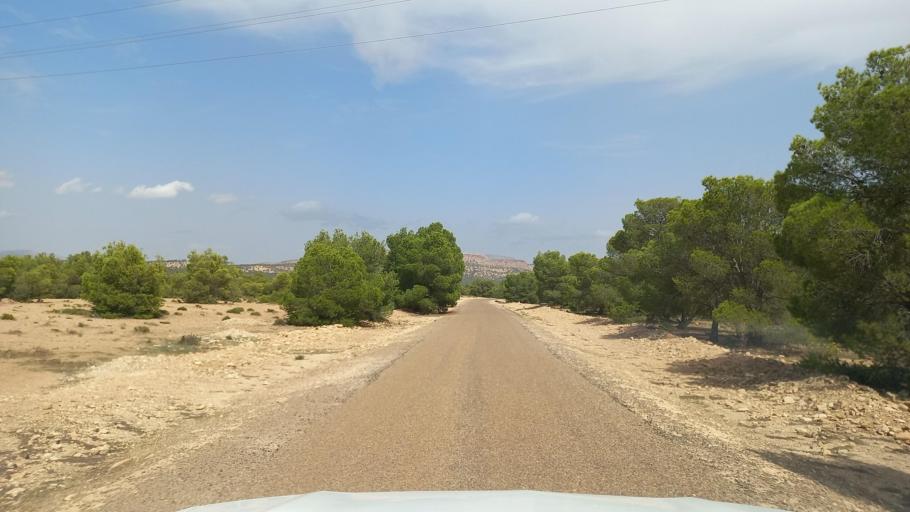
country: TN
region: Al Qasrayn
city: Sbiba
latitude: 35.3988
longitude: 8.9152
